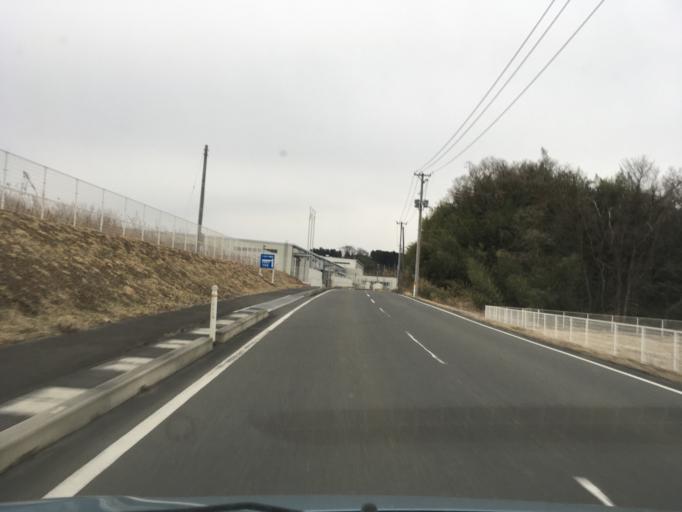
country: JP
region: Miyagi
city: Wakuya
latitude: 38.7018
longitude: 141.1687
